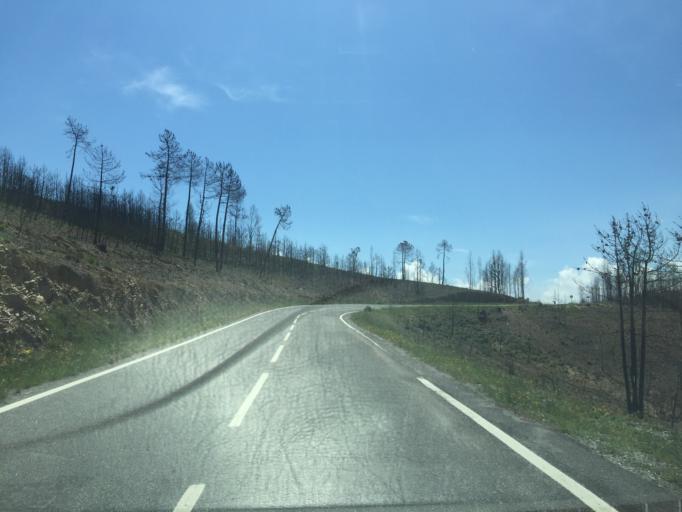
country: PT
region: Coimbra
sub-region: Pampilhosa da Serra
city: Pampilhosa da Serra
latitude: 40.0245
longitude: -7.9660
